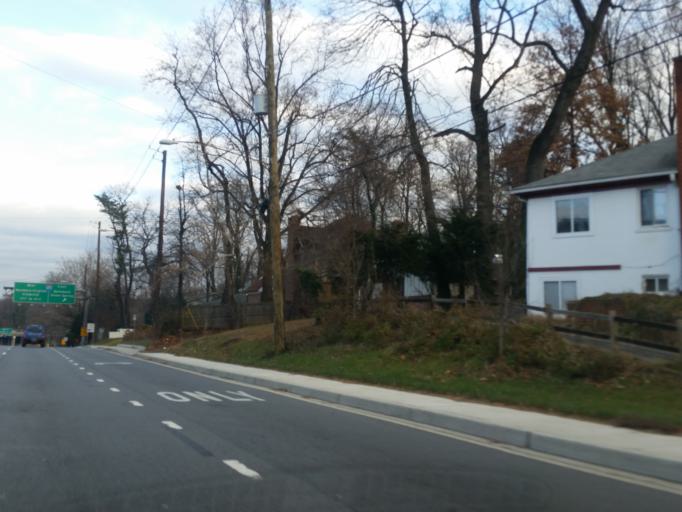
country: US
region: Maryland
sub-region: Montgomery County
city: South Kensington
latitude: 39.0018
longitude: -77.0771
